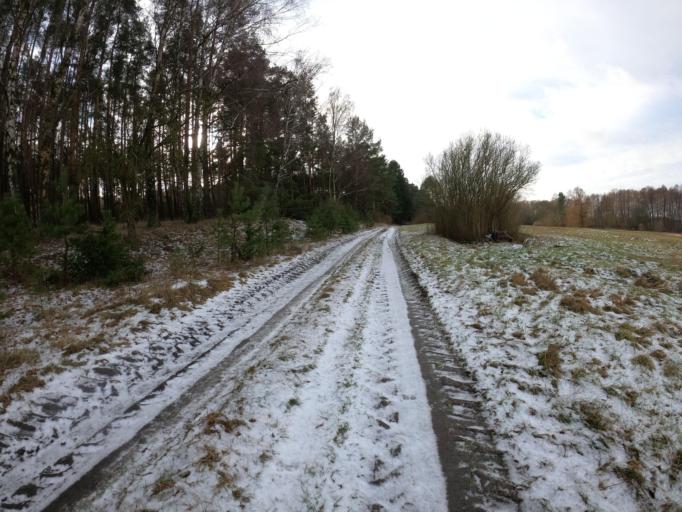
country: PL
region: Lubusz
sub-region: Powiat slubicki
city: Rzepin
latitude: 52.2781
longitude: 14.7959
